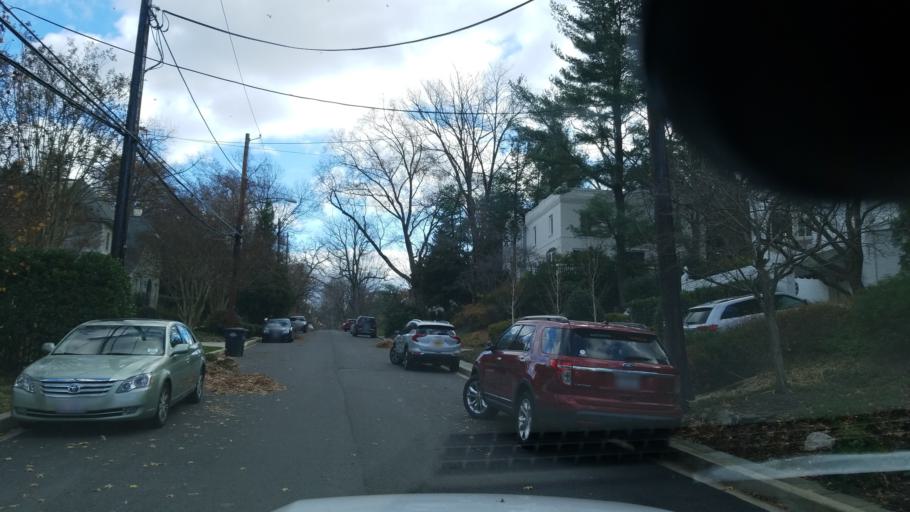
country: US
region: Maryland
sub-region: Montgomery County
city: Brookmont
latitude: 38.9315
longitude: -77.1020
